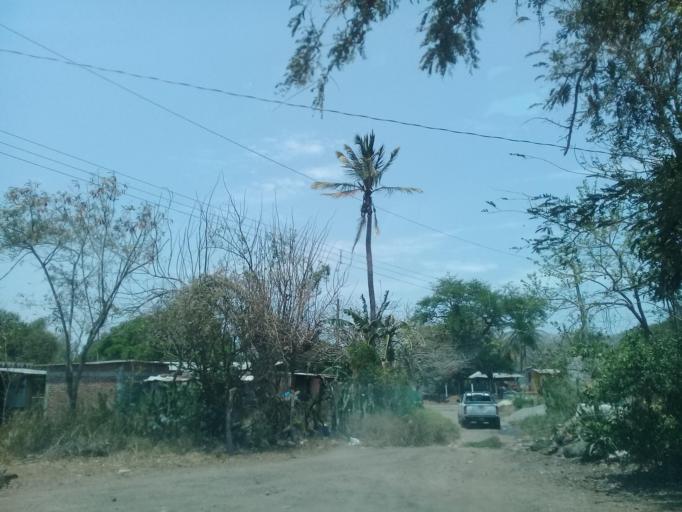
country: MX
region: Veracruz
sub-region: Veracruz
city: Delfino Victoria (Santa Fe)
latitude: 19.1699
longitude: -96.2917
